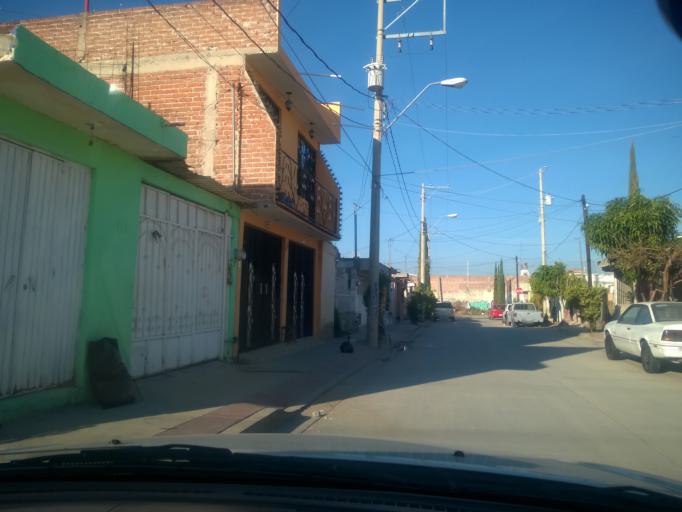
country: MX
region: Guanajuato
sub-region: Leon
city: San Jose de Duran (Los Troncoso)
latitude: 21.0689
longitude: -101.6355
